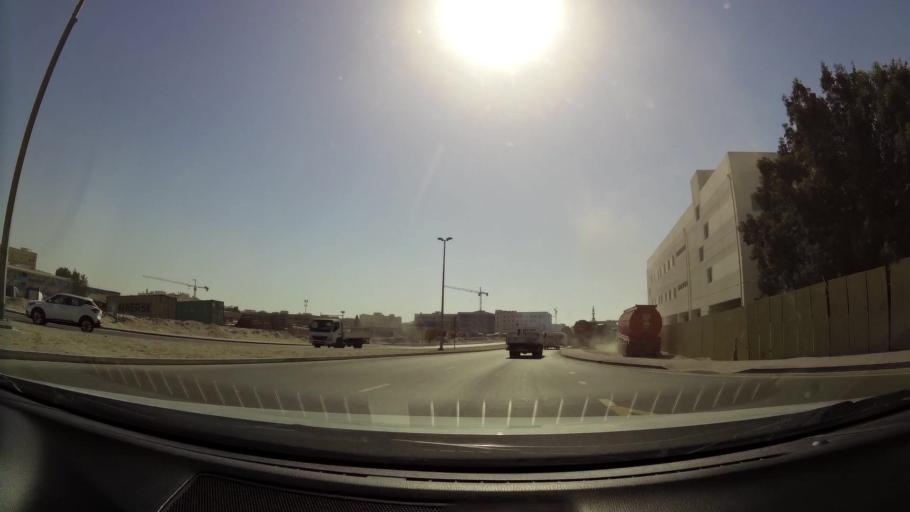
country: AE
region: Dubai
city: Dubai
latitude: 25.0047
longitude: 55.1111
